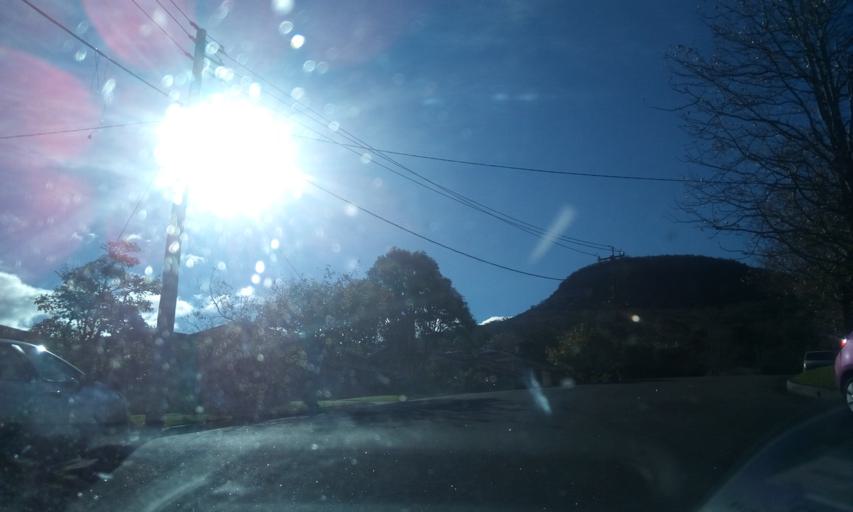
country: AU
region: New South Wales
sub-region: Wollongong
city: Mount Keira
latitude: -34.4168
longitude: 150.8569
